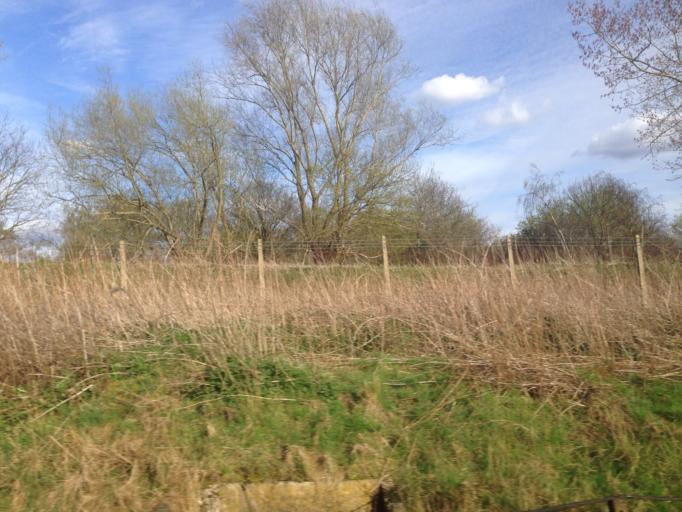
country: GB
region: England
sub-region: Greater London
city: Mitcham
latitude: 51.3998
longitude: -0.1590
